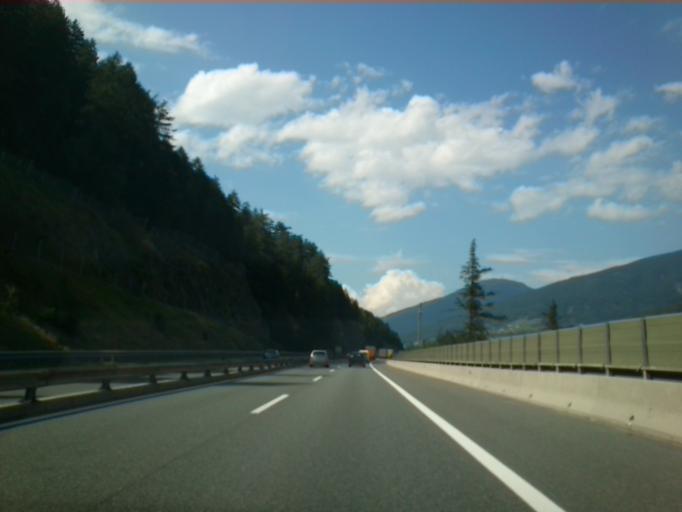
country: AT
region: Tyrol
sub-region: Politischer Bezirk Innsbruck Land
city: Matrei am Brenner
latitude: 47.1281
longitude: 11.4502
